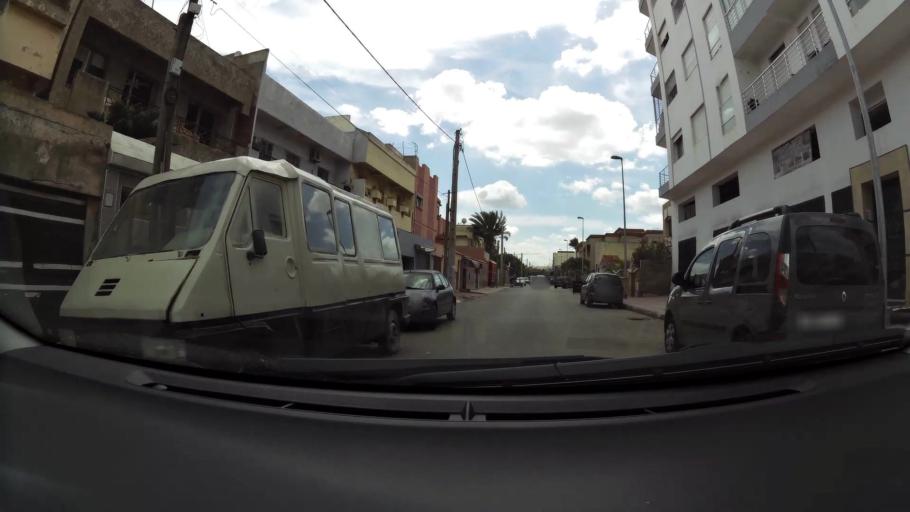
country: MA
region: Grand Casablanca
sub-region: Mediouna
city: Tit Mellil
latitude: 33.6174
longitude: -7.5342
